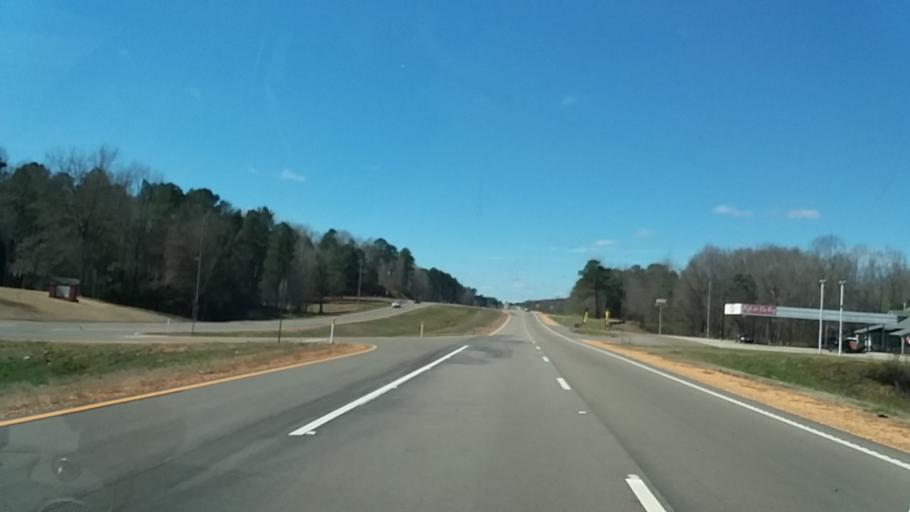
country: US
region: Mississippi
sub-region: Alcorn County
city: Farmington
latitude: 34.8651
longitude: -88.4169
